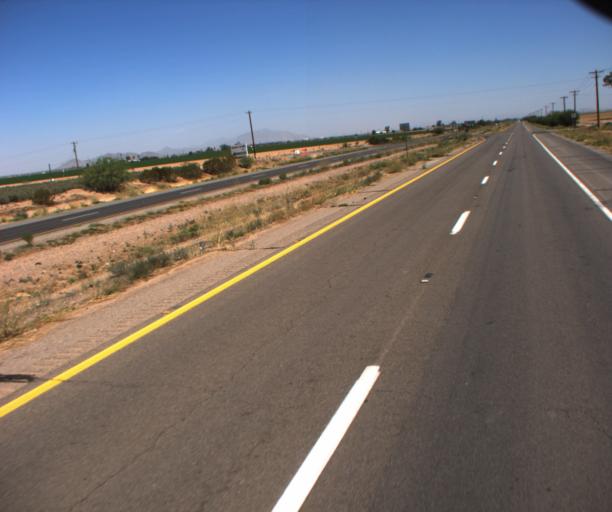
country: US
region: Arizona
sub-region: Pinal County
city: Maricopa
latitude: 32.8926
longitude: -112.0493
